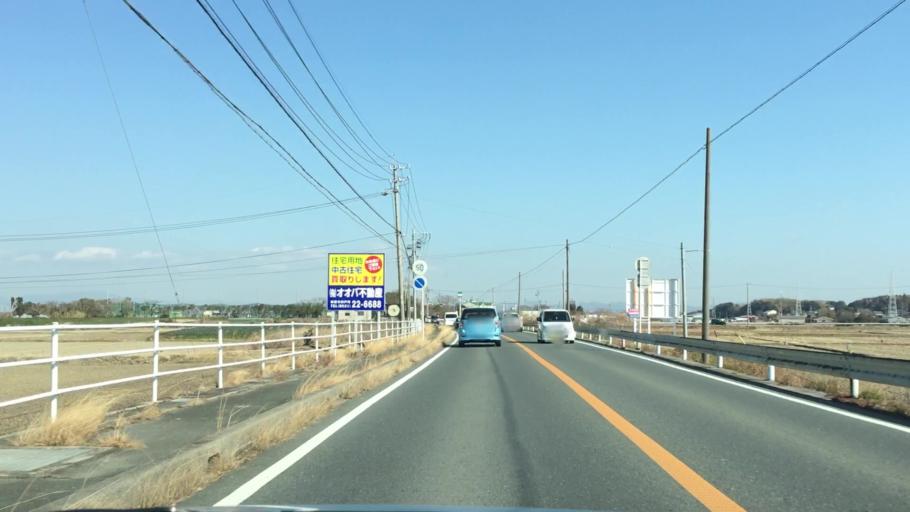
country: JP
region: Aichi
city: Tahara
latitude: 34.6784
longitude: 137.3112
